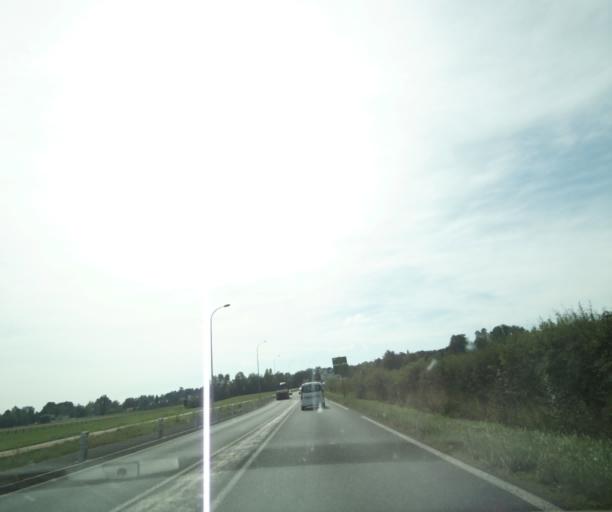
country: FR
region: Auvergne
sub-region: Departement de l'Allier
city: Bellerive-sur-Allier
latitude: 46.1297
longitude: 3.4018
